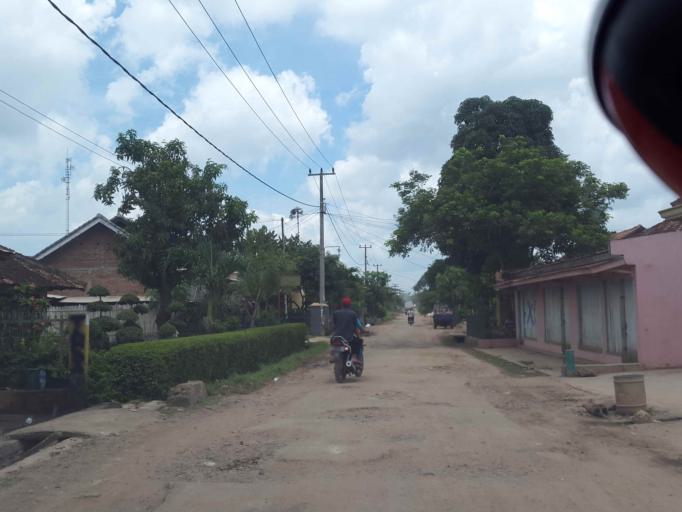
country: ID
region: Lampung
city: Natar
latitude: -5.3138
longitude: 105.2077
